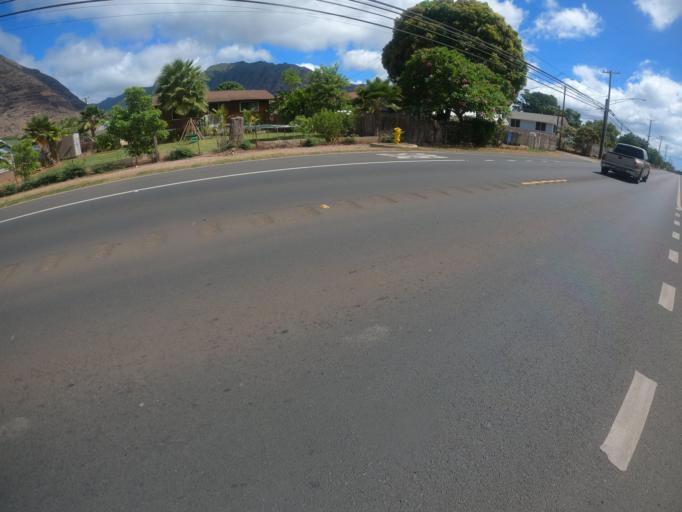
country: US
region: Hawaii
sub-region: Honolulu County
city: Makaha
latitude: 21.4737
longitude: -158.2180
